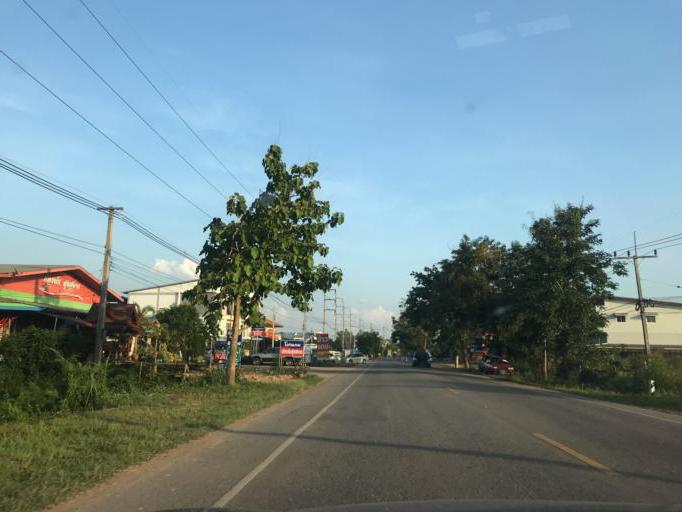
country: TH
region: Phayao
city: Chiang Kham
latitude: 19.5271
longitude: 100.2941
